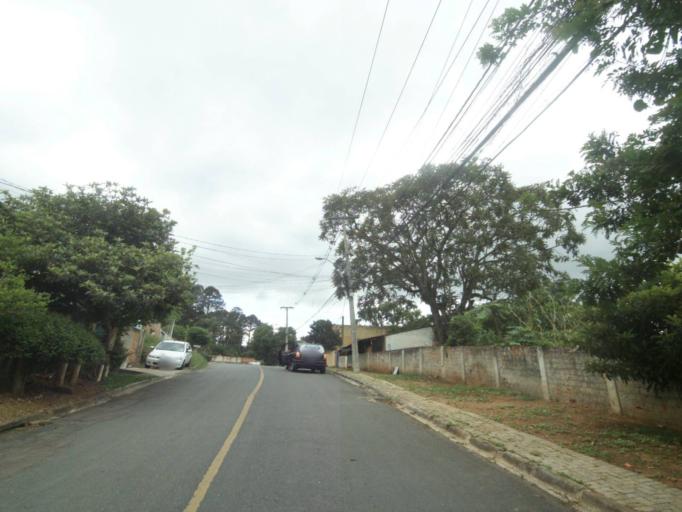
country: BR
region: Parana
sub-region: Curitiba
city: Curitiba
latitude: -25.3871
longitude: -49.2880
